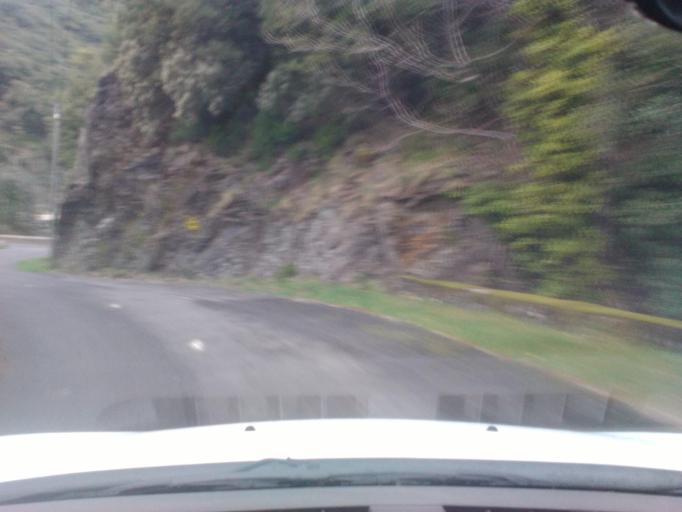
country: FR
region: Languedoc-Roussillon
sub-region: Departement du Gard
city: Valleraugue
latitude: 44.1073
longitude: 3.6403
